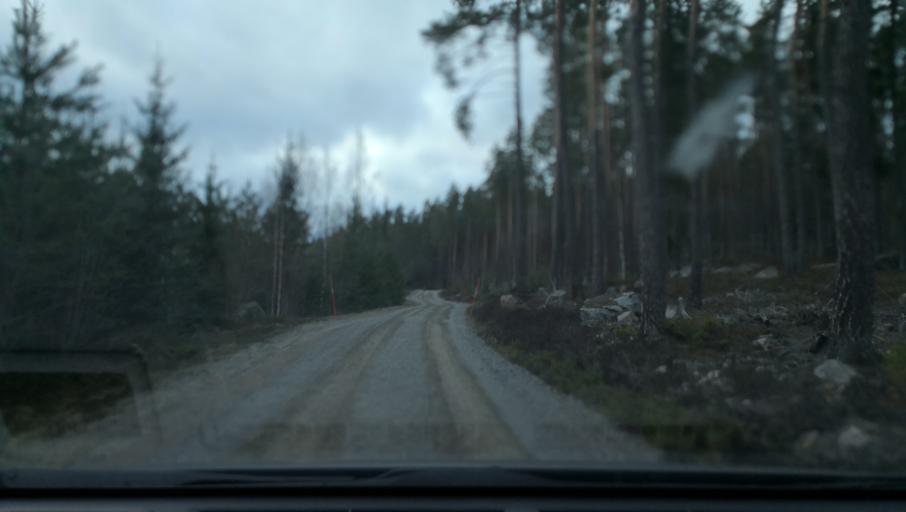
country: SE
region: Vaestmanland
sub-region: Kopings Kommun
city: Kolsva
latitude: 59.5661
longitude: 15.8234
